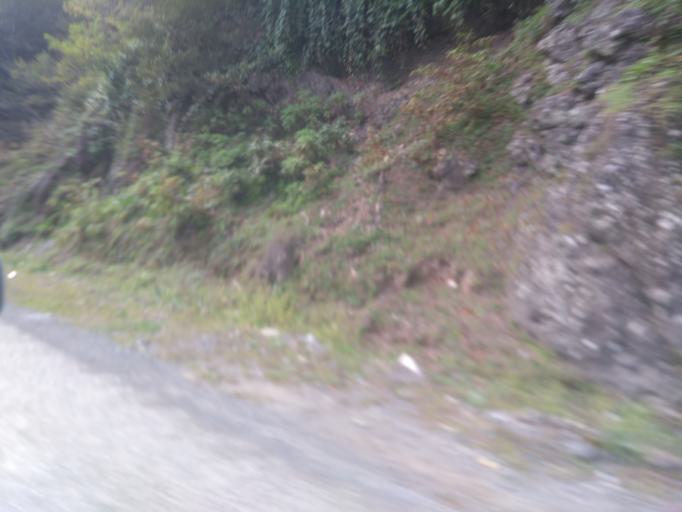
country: TR
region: Artvin
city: Muratli
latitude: 41.5510
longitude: 41.7990
